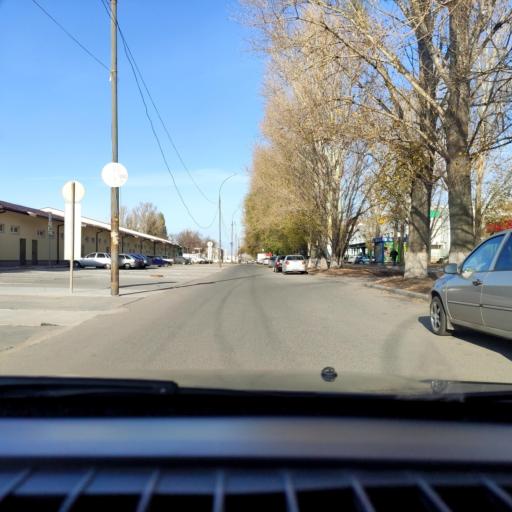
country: RU
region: Samara
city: Tol'yatti
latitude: 53.5226
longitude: 49.2811
